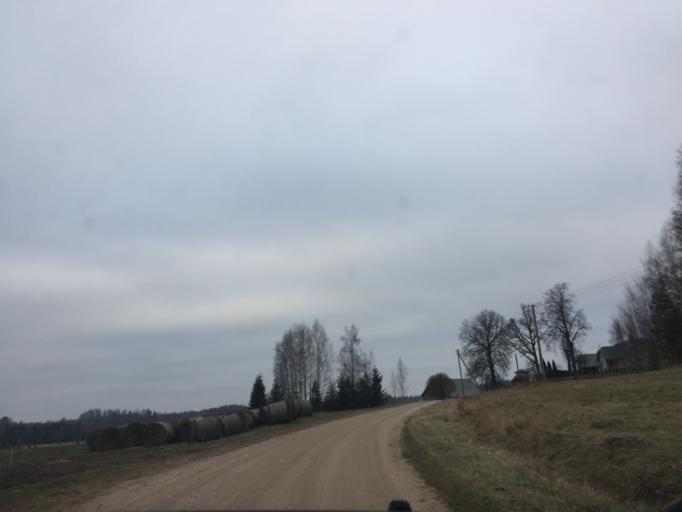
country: LV
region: Ligatne
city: Ligatne
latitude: 57.2218
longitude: 25.1194
